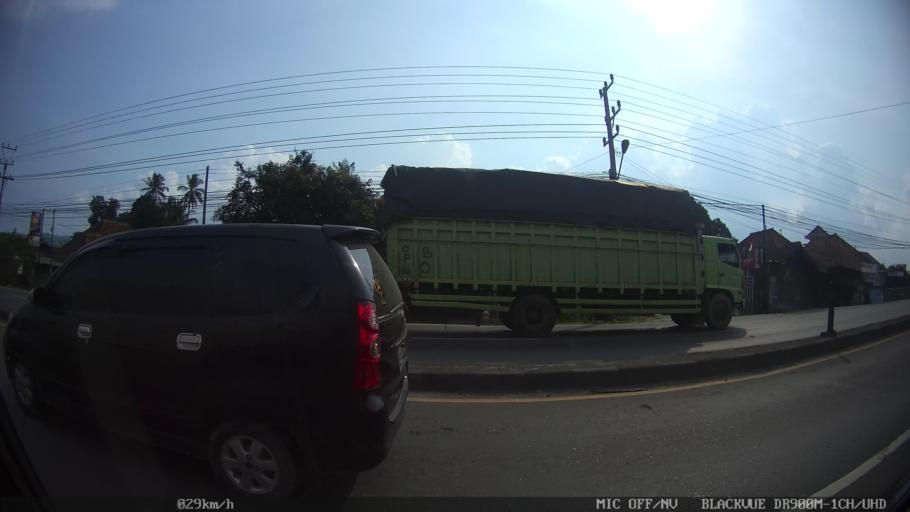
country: ID
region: Lampung
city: Kedaton
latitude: -5.3565
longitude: 105.2207
